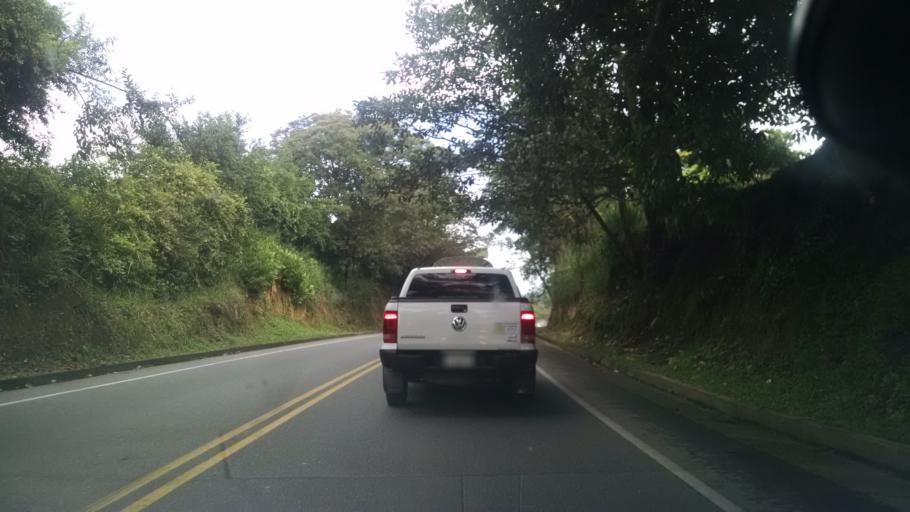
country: CO
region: Caldas
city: Palestina
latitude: 5.0841
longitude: -75.6515
